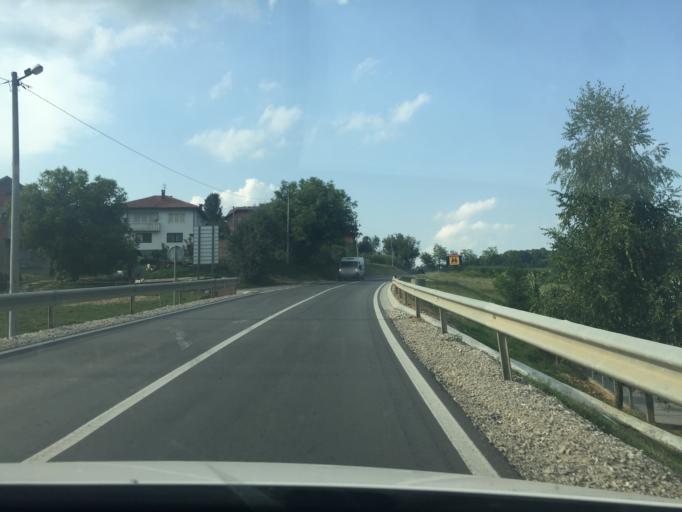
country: BA
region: Federation of Bosnia and Herzegovina
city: Mionica
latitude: 44.8261
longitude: 18.4522
